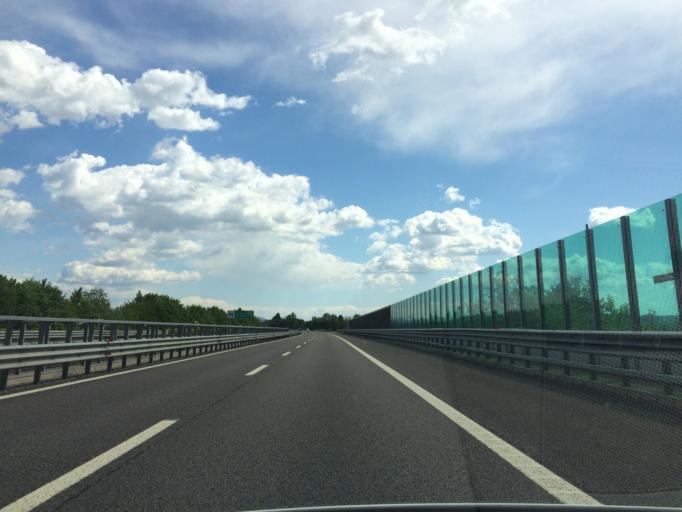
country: IT
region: Veneto
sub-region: Provincia di Vicenza
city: Villaggio Montegrappa
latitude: 45.5582
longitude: 11.6150
